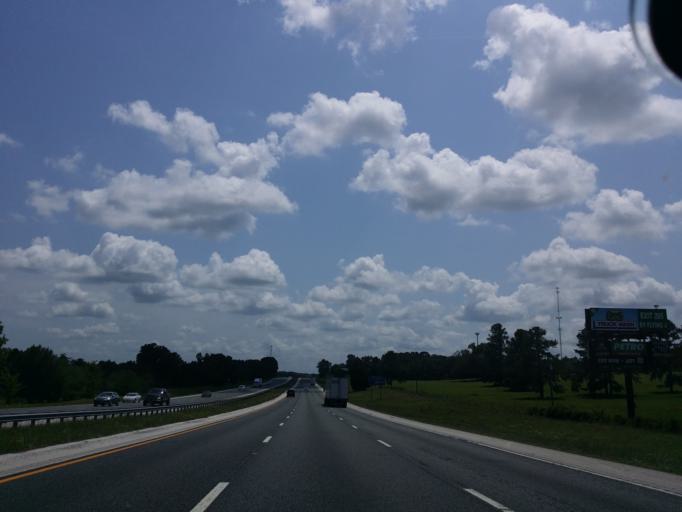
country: US
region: Florida
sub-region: Marion County
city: Citra
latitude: 29.4164
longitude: -82.2548
